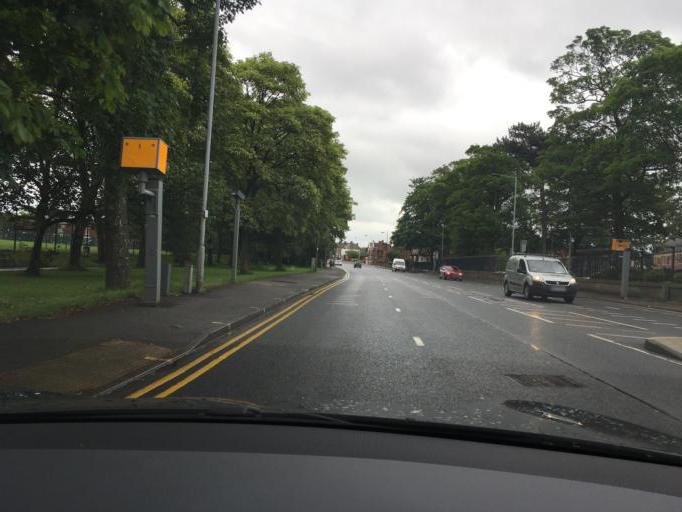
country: GB
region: England
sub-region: Borough of Stockport
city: Stockport
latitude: 53.3907
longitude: -2.1422
